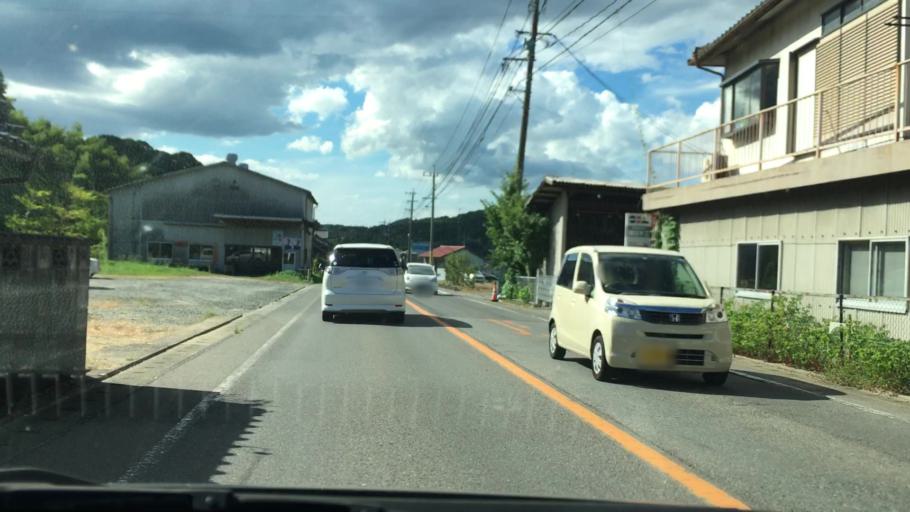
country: JP
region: Saga Prefecture
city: Takeocho-takeo
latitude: 33.1919
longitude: 129.9822
